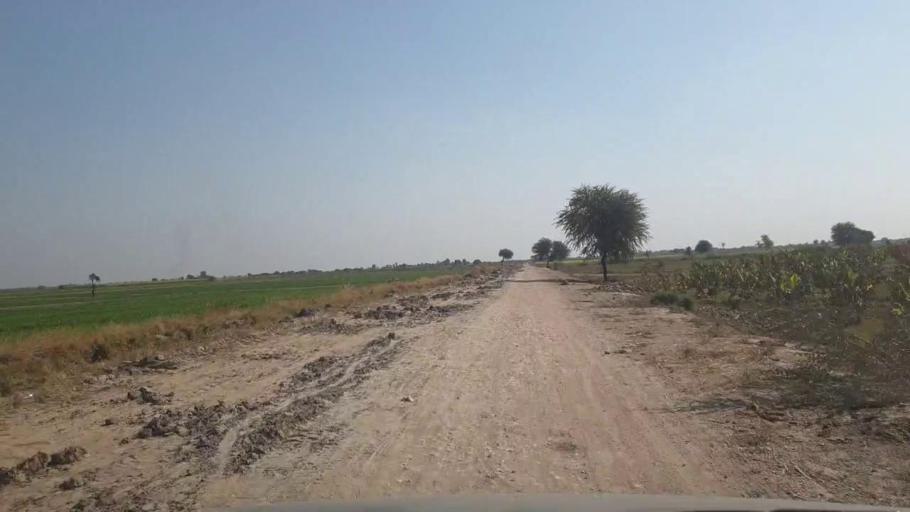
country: PK
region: Sindh
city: Chambar
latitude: 25.3224
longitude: 68.8689
